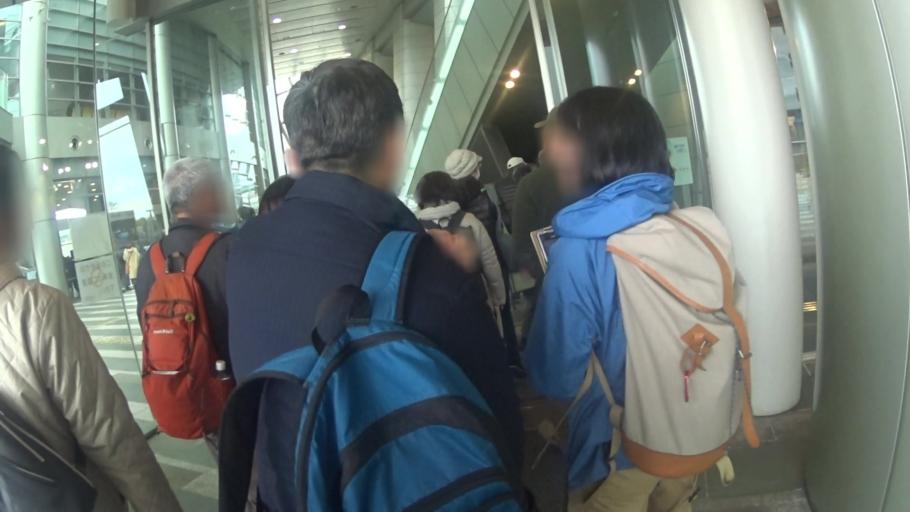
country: JP
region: Osaka
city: Osaka-shi
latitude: 34.6815
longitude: 135.5205
